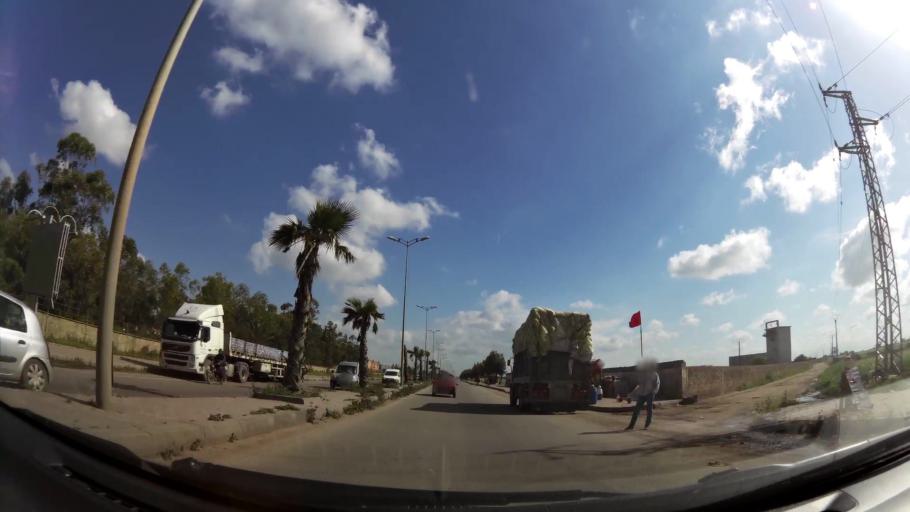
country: MA
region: Grand Casablanca
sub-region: Mediouna
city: Mediouna
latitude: 33.4519
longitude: -7.5214
